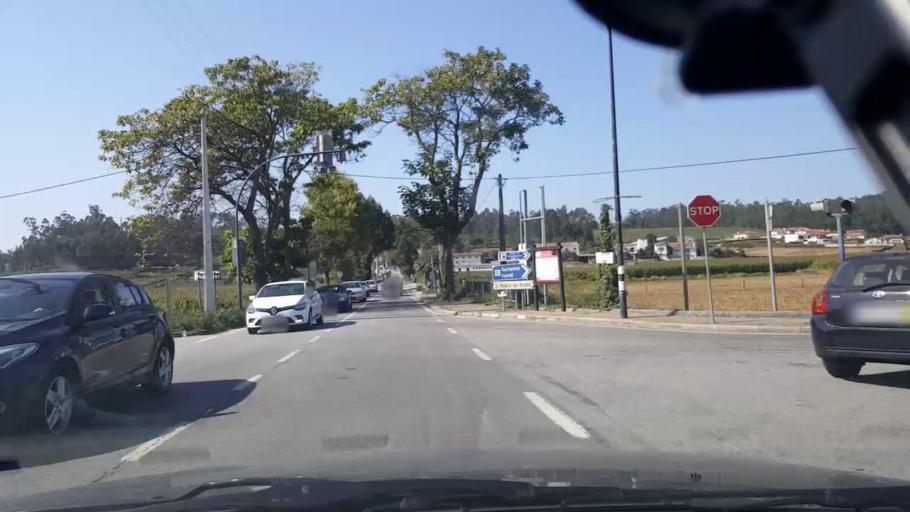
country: PT
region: Porto
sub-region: Povoa de Varzim
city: Pedroso
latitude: 41.4121
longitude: -8.6648
